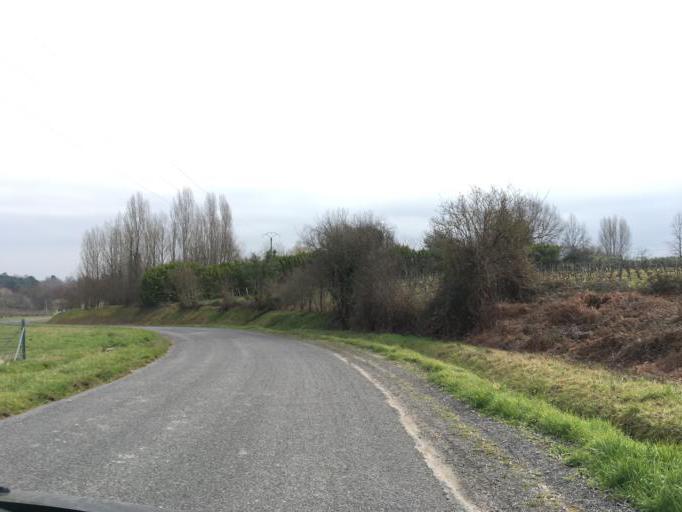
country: FR
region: Aquitaine
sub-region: Departement de la Gironde
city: Saint-Ciers-sur-Gironde
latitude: 45.3296
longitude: -0.5918
